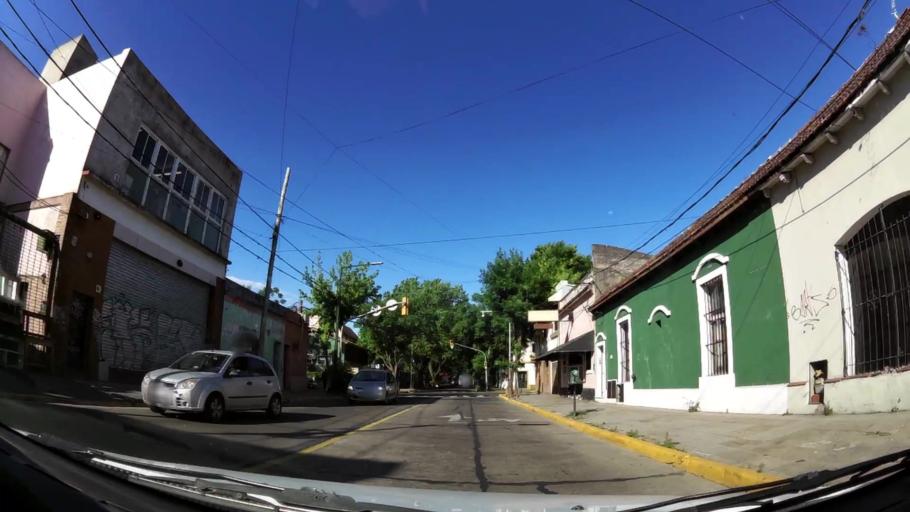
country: AR
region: Buenos Aires
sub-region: Partido de San Isidro
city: San Isidro
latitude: -34.4678
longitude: -58.5161
